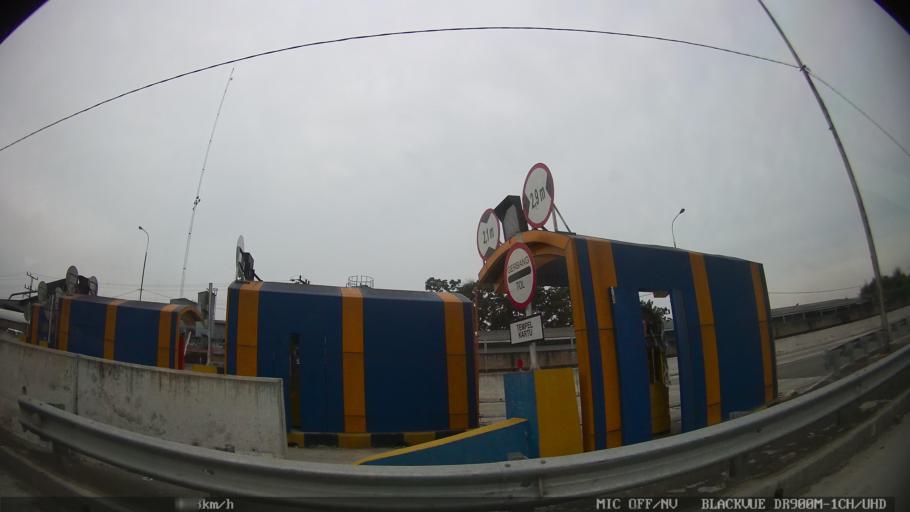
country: ID
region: North Sumatra
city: Deli Tua
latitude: 3.5407
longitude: 98.7238
